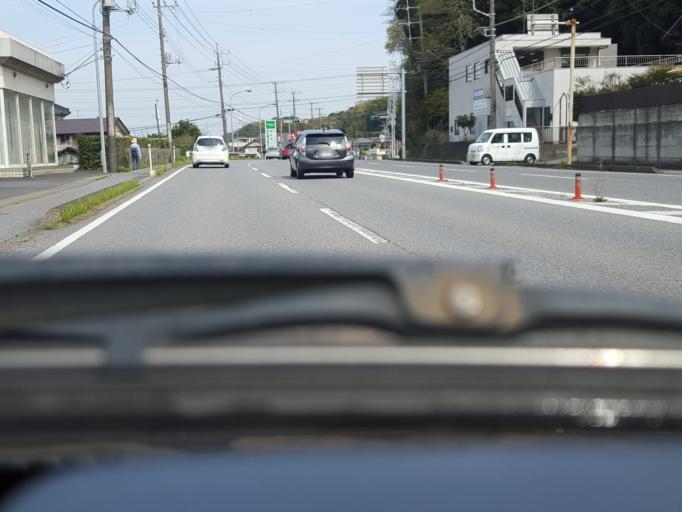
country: JP
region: Chiba
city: Ichihara
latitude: 35.4591
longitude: 140.0484
